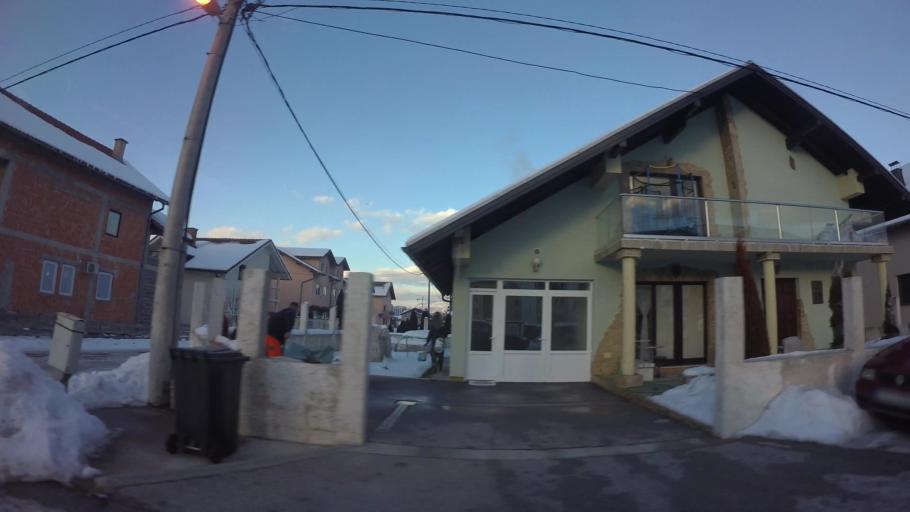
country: BA
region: Federation of Bosnia and Herzegovina
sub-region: Kanton Sarajevo
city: Sarajevo
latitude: 43.8116
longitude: 18.3617
